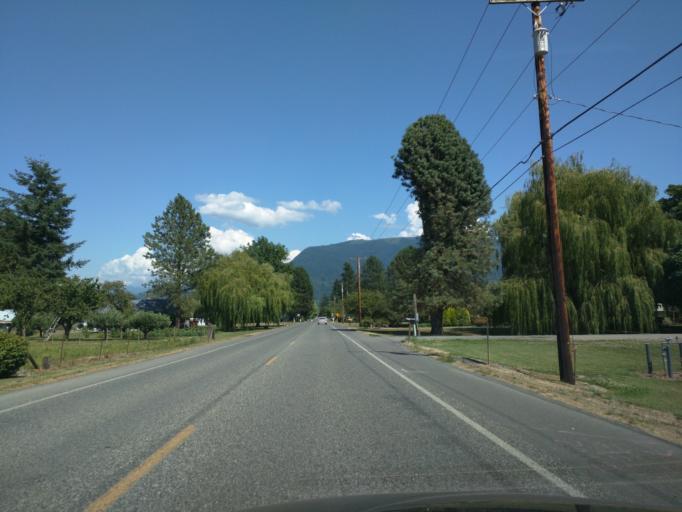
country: US
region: Washington
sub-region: Whatcom County
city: Nooksack
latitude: 48.9202
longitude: -122.3180
